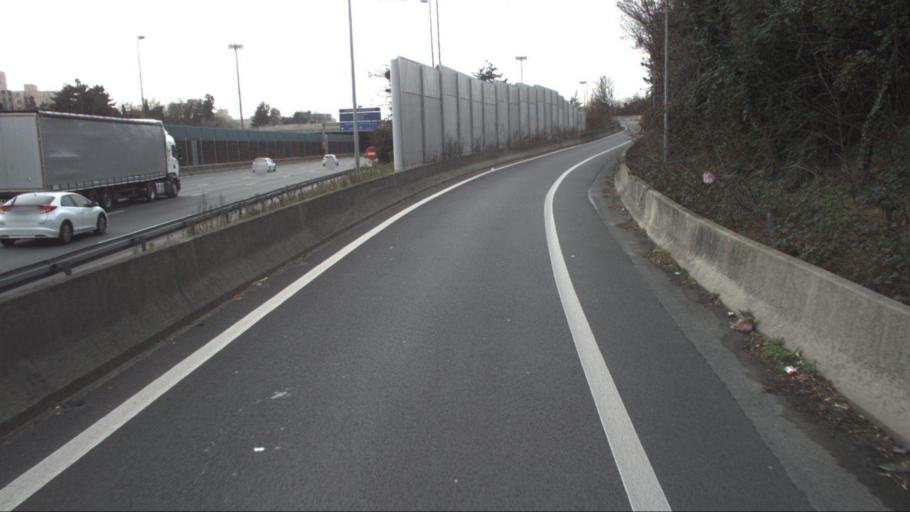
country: FR
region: Ile-de-France
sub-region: Departement du Val-de-Marne
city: Maisons-Alfort
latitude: 48.8020
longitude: 2.4474
